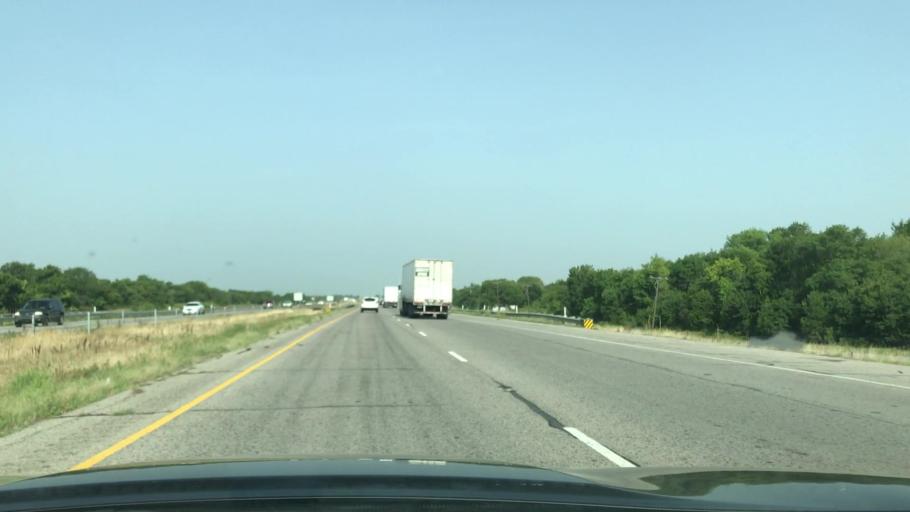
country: US
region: Texas
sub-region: Kaufman County
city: Talty
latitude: 32.7394
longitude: -96.3734
